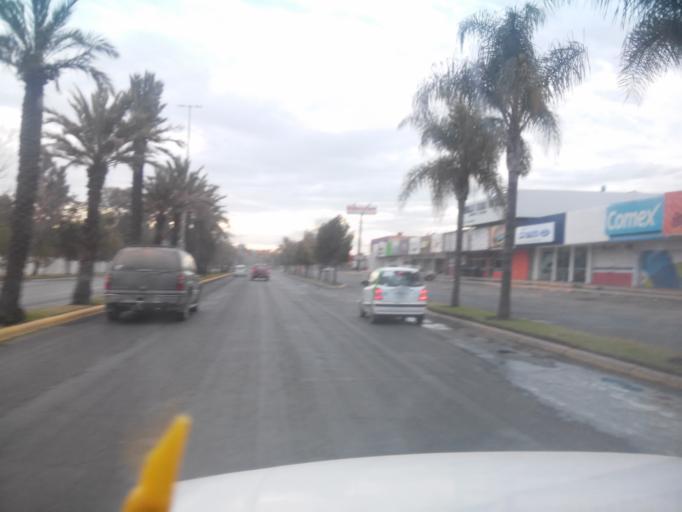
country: MX
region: Durango
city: Victoria de Durango
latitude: 24.0083
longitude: -104.6605
